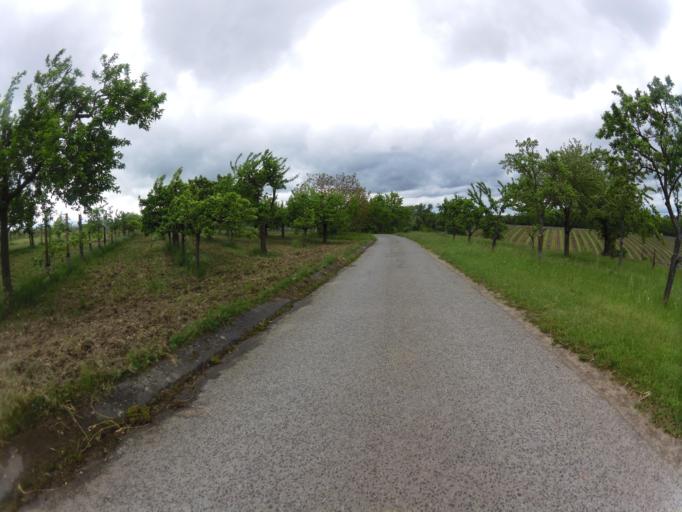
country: DE
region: Bavaria
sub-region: Regierungsbezirk Unterfranken
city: Sommerach
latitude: 49.8486
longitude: 10.2074
